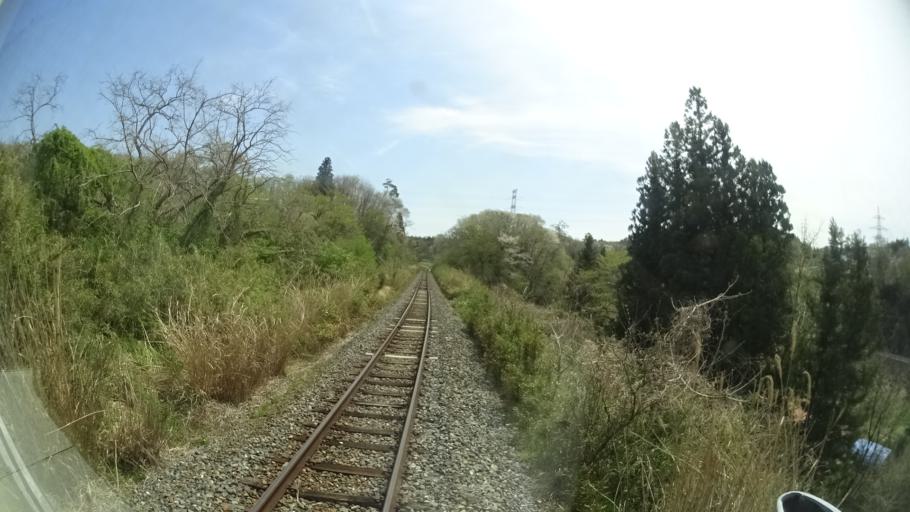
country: JP
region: Iwate
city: Ichinoseki
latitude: 38.9931
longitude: 141.2970
